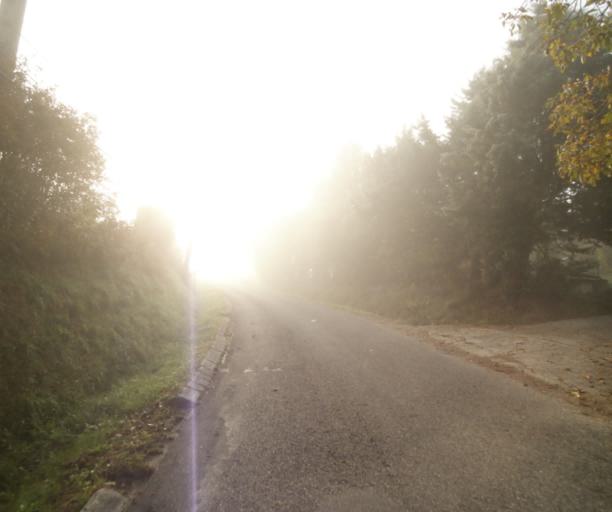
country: FR
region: Midi-Pyrenees
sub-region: Departement du Tarn-et-Garonne
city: Nohic
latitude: 43.9067
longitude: 1.4601
